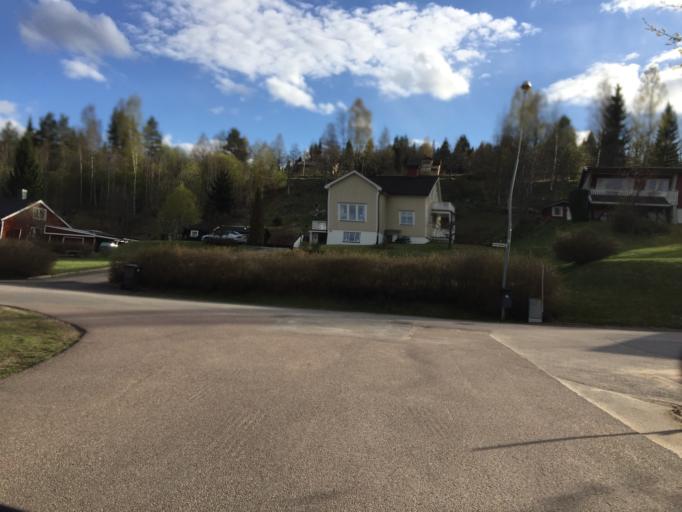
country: SE
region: Dalarna
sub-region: Ludvika Kommun
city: Ludvika
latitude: 60.1318
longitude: 15.1605
